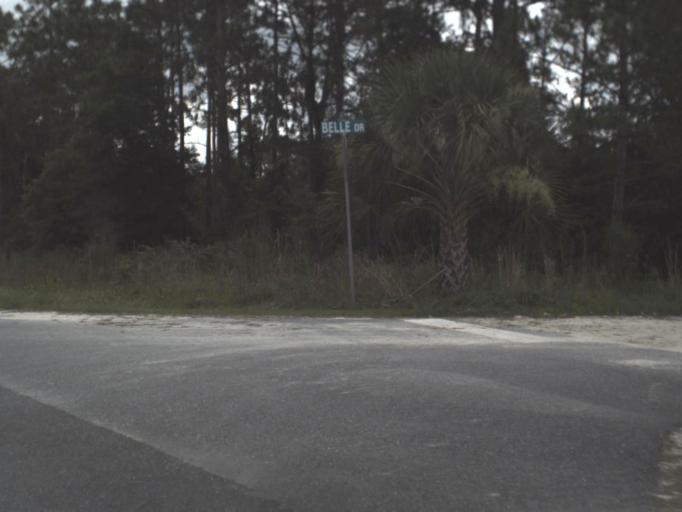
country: US
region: Florida
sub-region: Putnam County
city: Palatka
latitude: 29.5815
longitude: -81.6178
